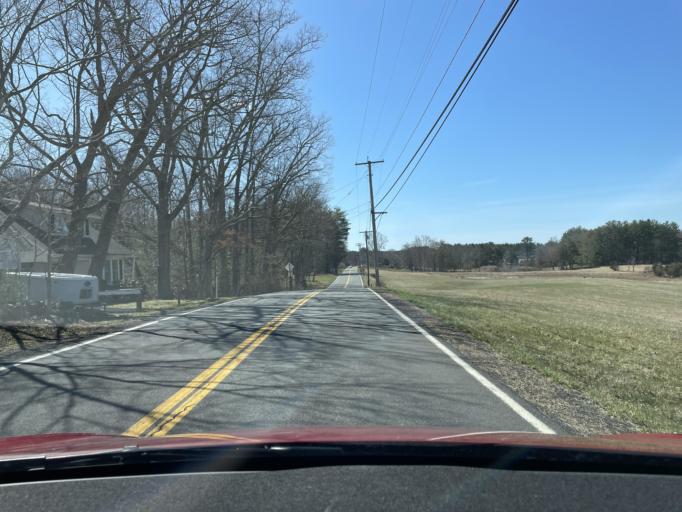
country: US
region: New York
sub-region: Ulster County
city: Zena
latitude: 42.0514
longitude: -74.0195
